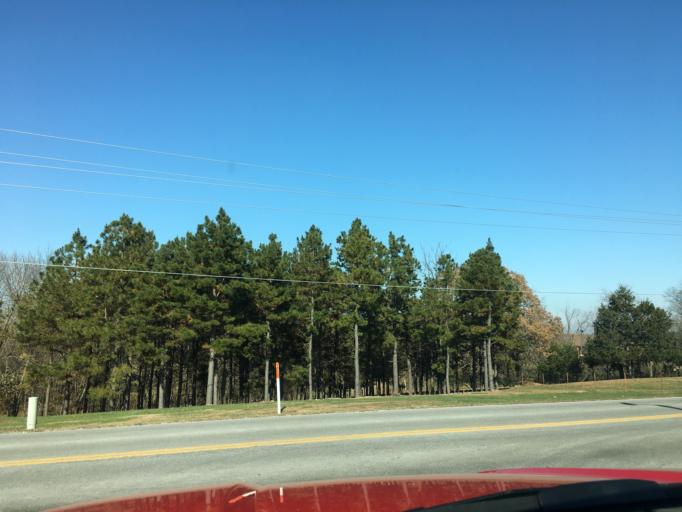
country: US
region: Missouri
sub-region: Cole County
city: Wardsville
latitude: 38.4853
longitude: -92.1857
